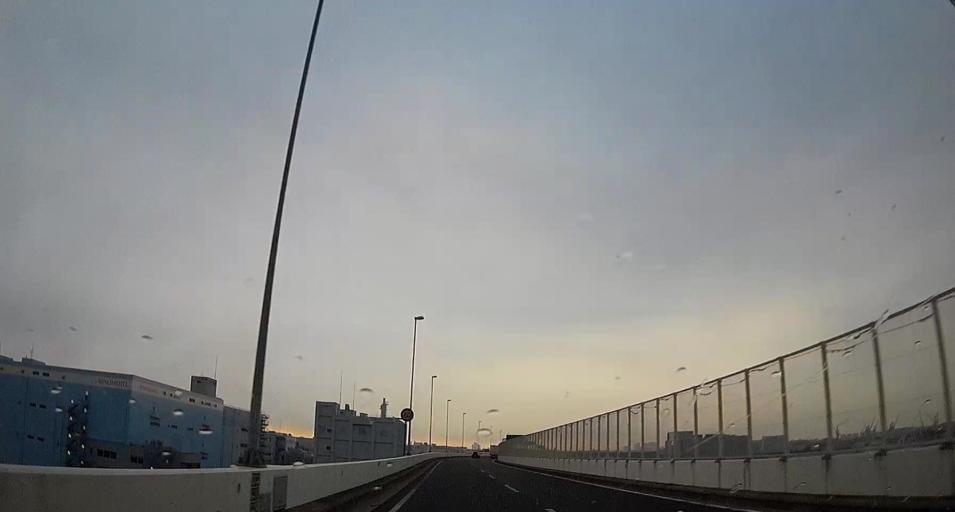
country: JP
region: Kanagawa
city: Yokohama
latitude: 35.4761
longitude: 139.6754
